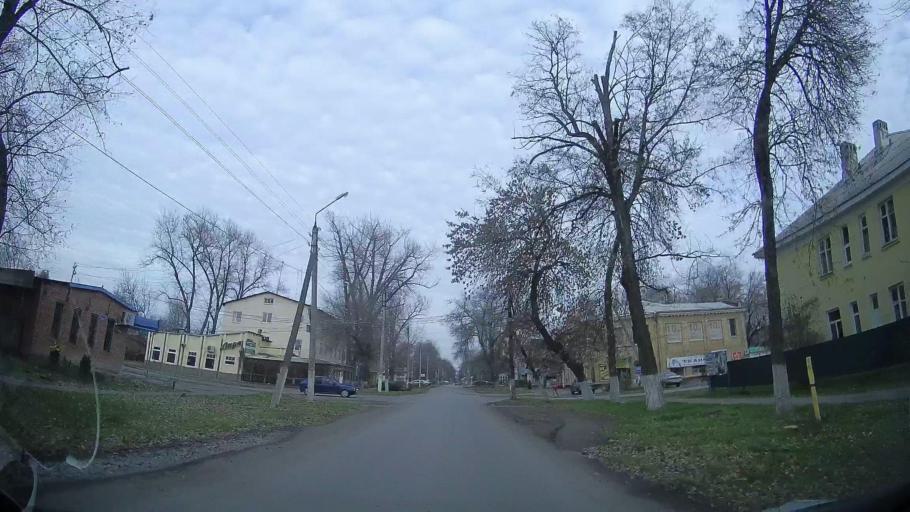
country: RU
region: Rostov
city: Zernograd
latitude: 46.8497
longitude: 40.3096
